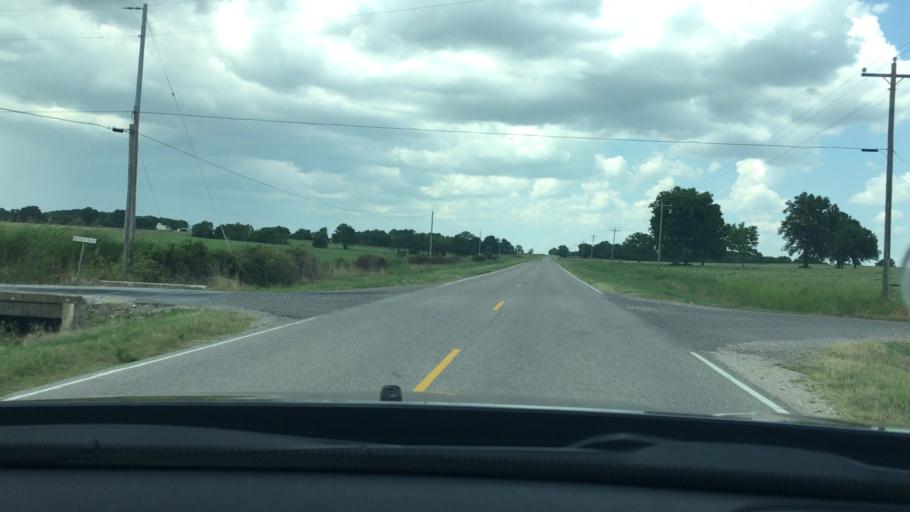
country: US
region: Oklahoma
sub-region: Johnston County
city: Tishomingo
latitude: 34.4627
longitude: -96.6360
